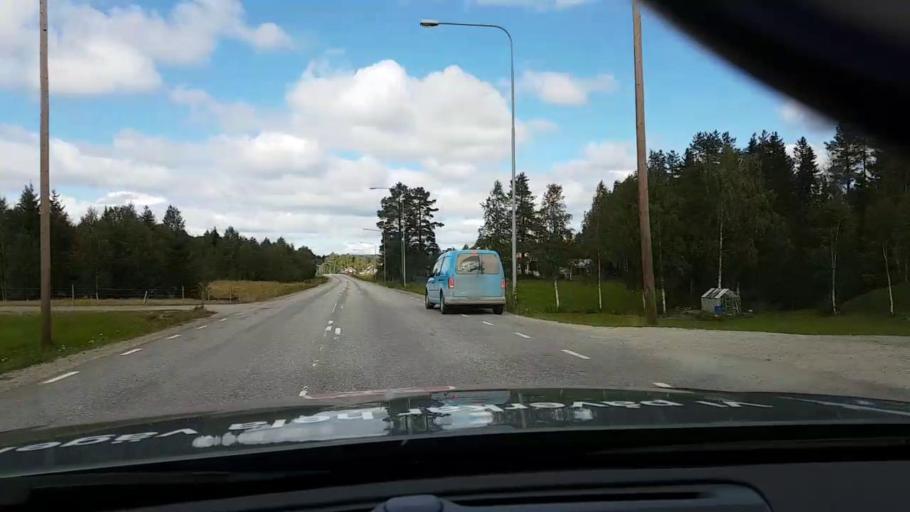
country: SE
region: Vaesternorrland
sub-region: OErnskoeldsviks Kommun
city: Bredbyn
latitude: 63.4769
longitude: 18.0944
